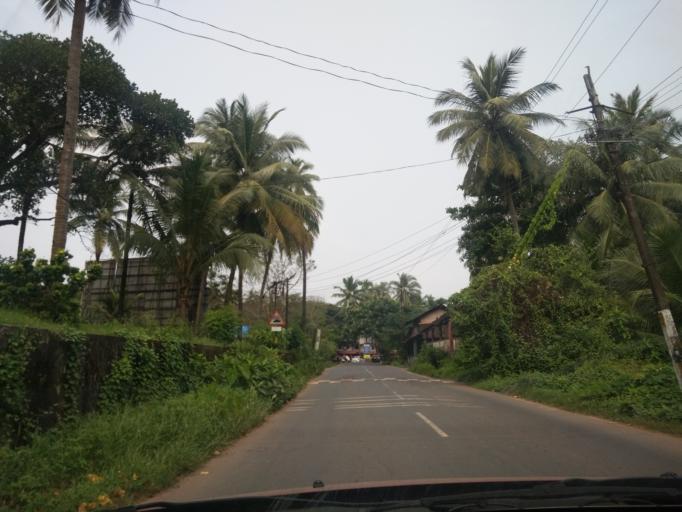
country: IN
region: Goa
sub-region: North Goa
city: Goa Velha
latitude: 15.4260
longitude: 73.8992
